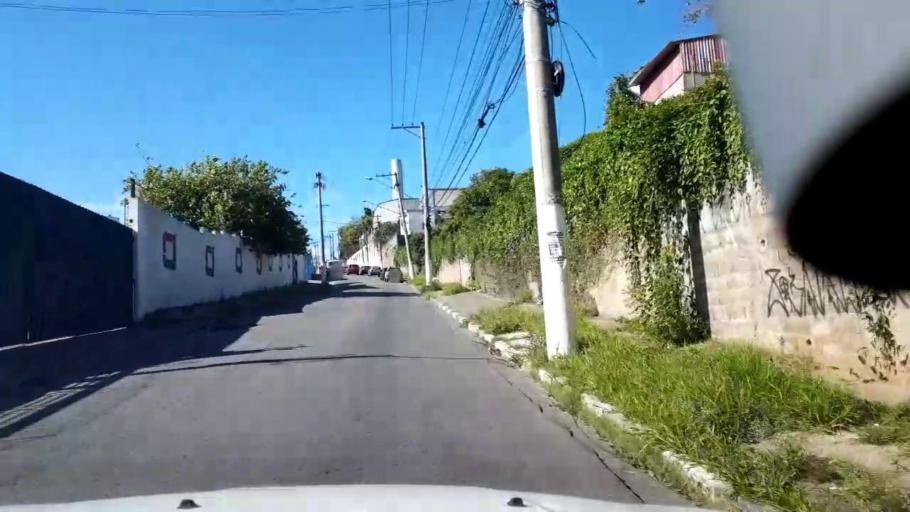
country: BR
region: Sao Paulo
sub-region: Ferraz De Vasconcelos
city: Ferraz de Vasconcelos
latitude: -23.5296
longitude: -46.3900
